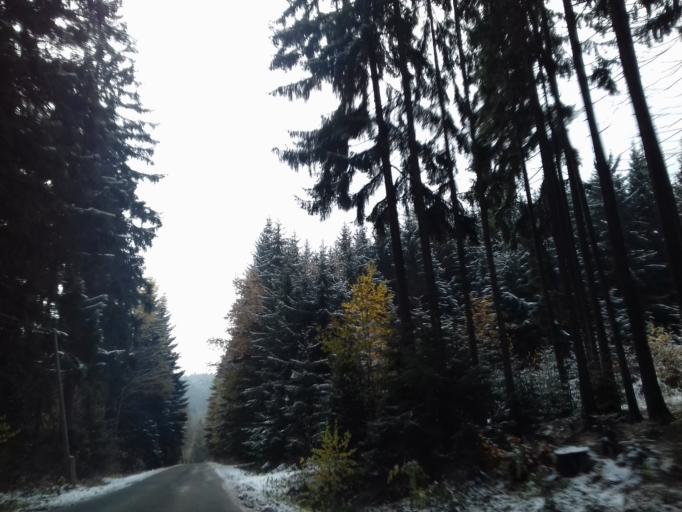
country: CZ
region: Plzensky
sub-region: Okres Domazlice
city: Klenci pod Cerchovem
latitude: 49.4354
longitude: 12.7982
